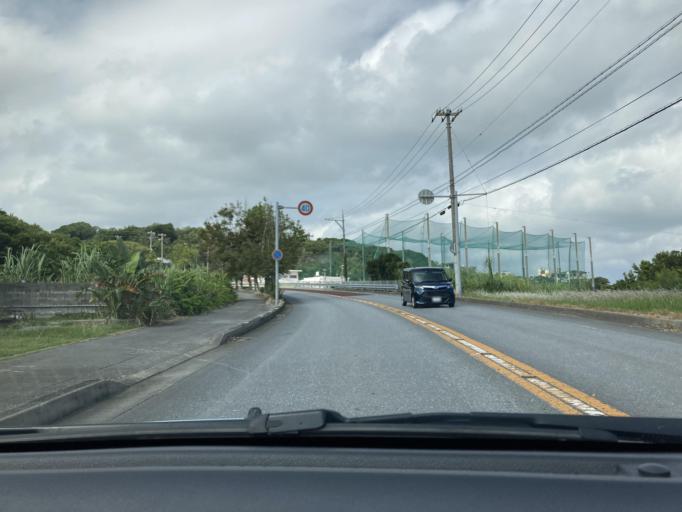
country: JP
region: Okinawa
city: Ishikawa
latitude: 26.4087
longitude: 127.8361
